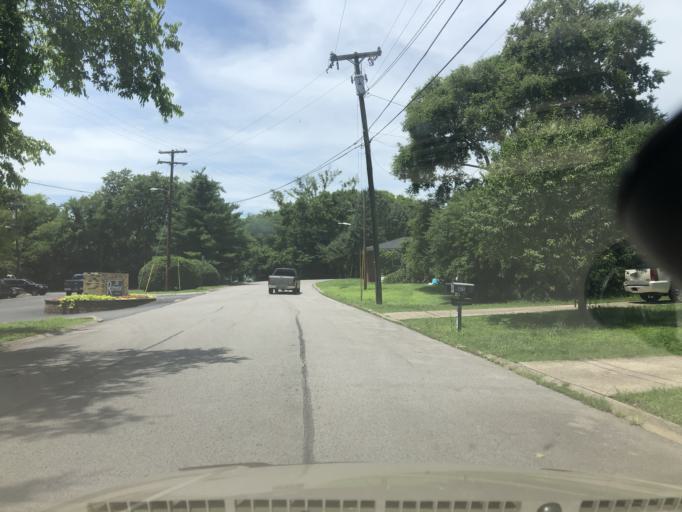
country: US
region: Tennessee
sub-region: Davidson County
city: Lakewood
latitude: 36.2509
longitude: -86.7007
